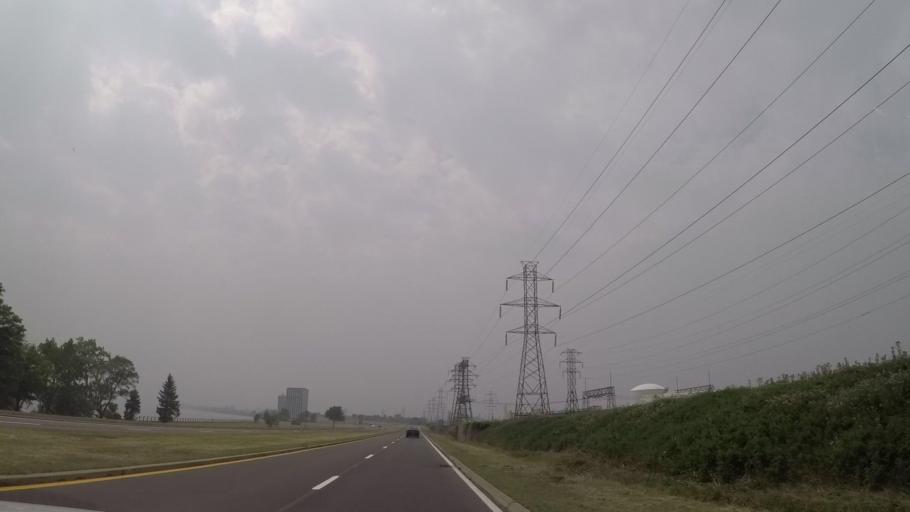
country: US
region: New York
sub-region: Niagara County
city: Niagara Falls
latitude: 43.0760
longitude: -79.0086
